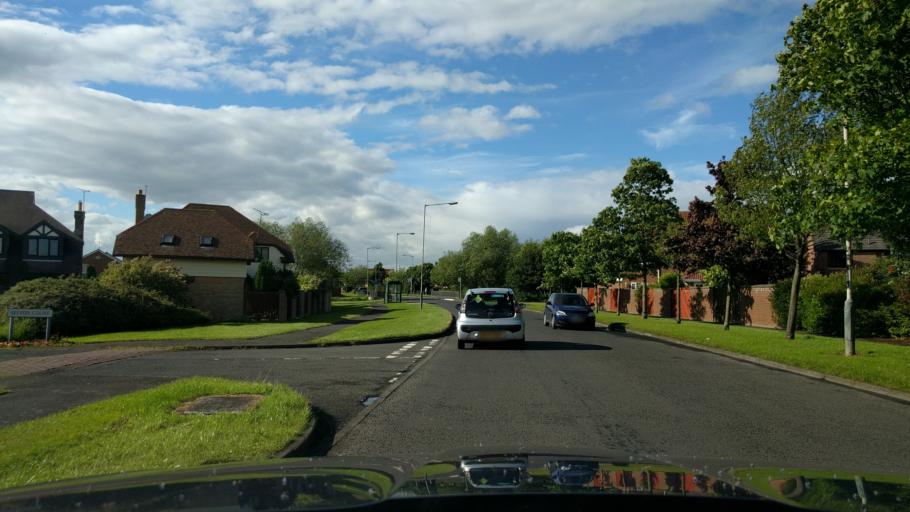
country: GB
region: England
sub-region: Northumberland
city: Cramlington
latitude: 55.0995
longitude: -1.5769
